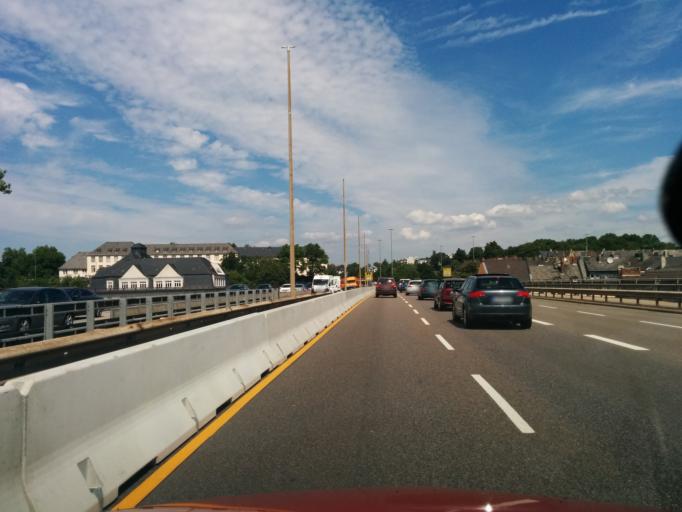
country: DE
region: Rheinland-Pfalz
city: Koblenz
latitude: 50.3655
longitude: 7.5880
